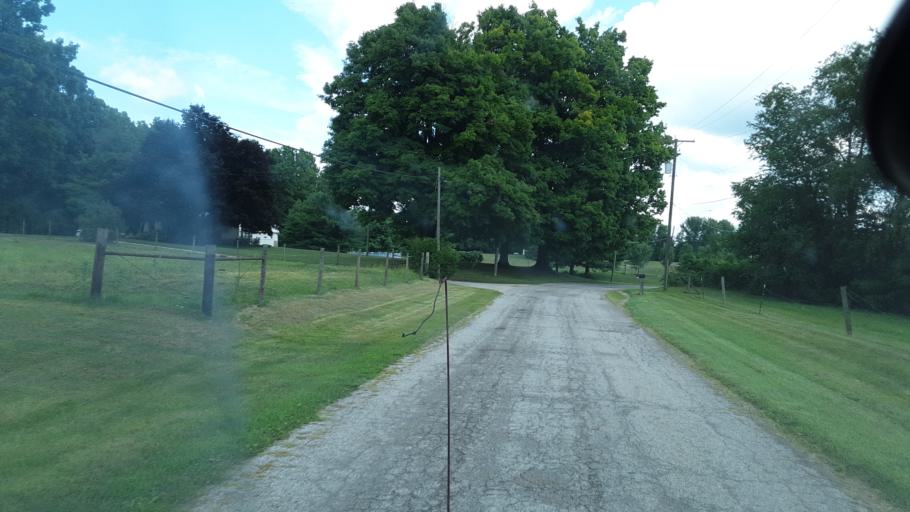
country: US
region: Ohio
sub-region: Licking County
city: Utica
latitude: 40.2674
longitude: -82.3958
